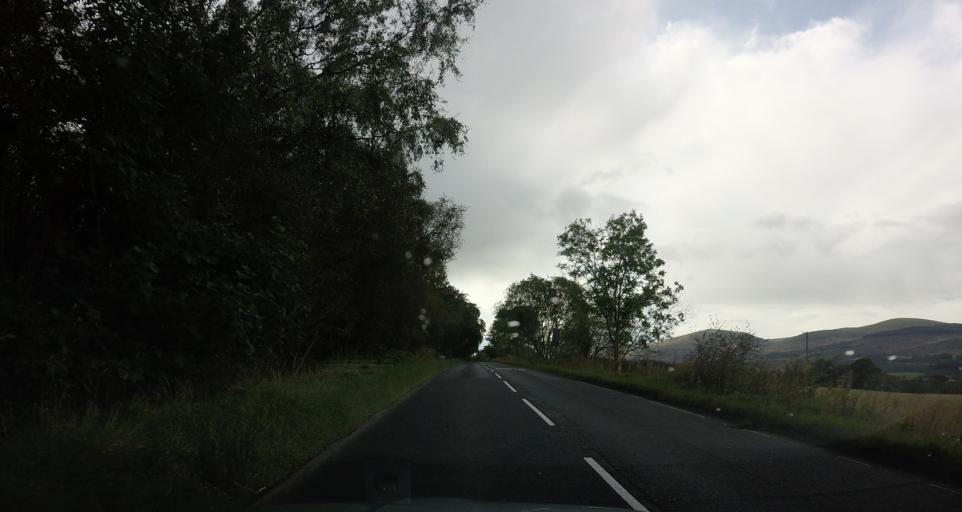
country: GB
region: Scotland
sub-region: Fife
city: Saline
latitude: 56.1619
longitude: -3.5961
